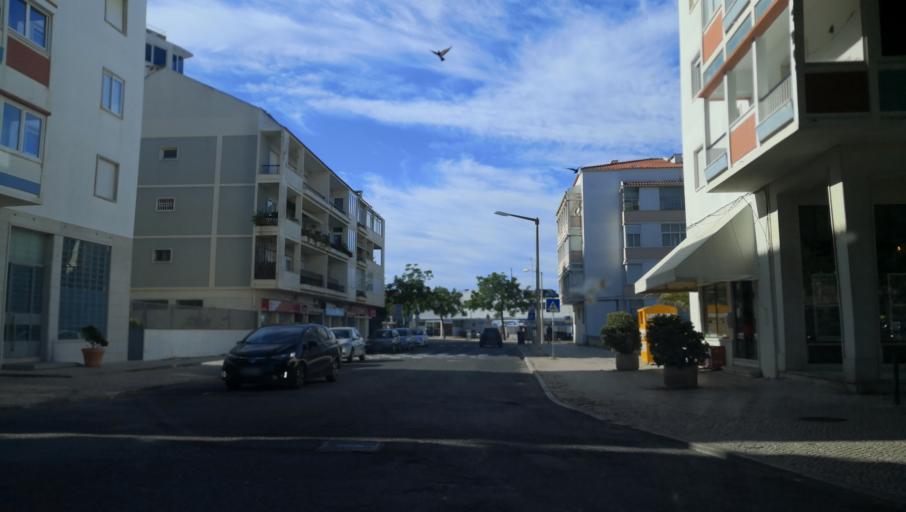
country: PT
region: Lisbon
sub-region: Cascais
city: Parede
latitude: 38.6838
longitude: -9.3428
